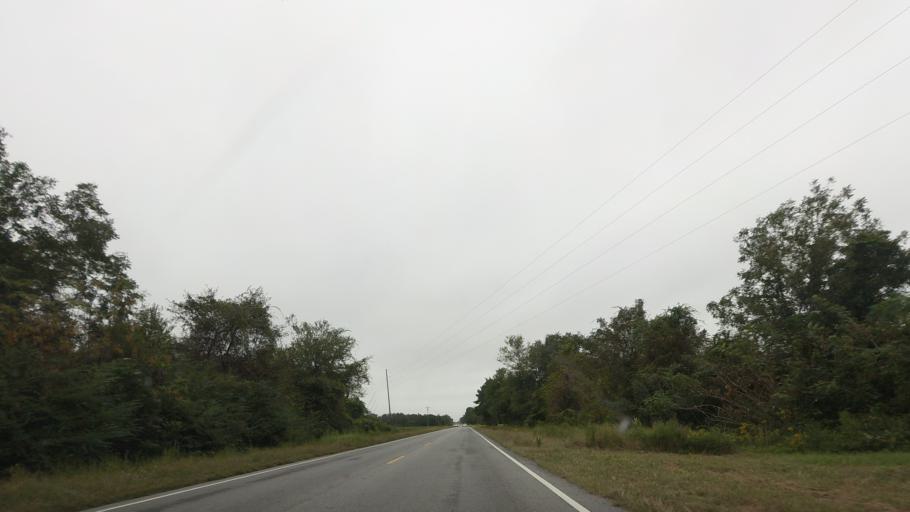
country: US
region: Georgia
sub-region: Berrien County
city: Nashville
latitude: 31.3313
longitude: -83.2299
